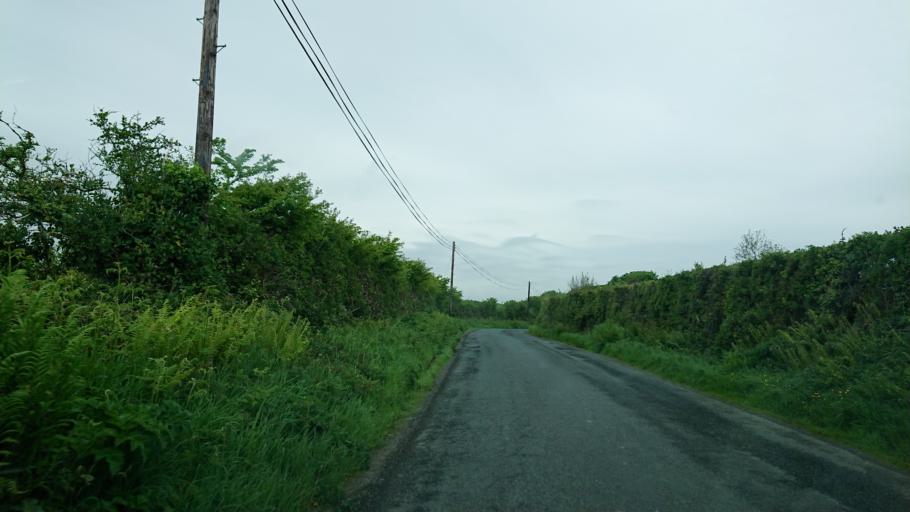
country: IE
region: Munster
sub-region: Waterford
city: Dunmore East
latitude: 52.2210
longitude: -7.0350
